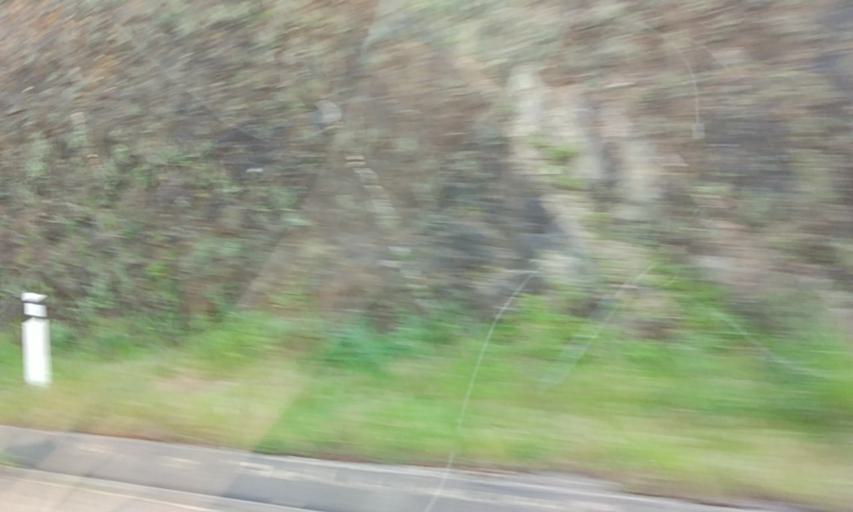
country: PT
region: Portalegre
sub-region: Elvas
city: Elvas
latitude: 38.9016
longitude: -7.1370
